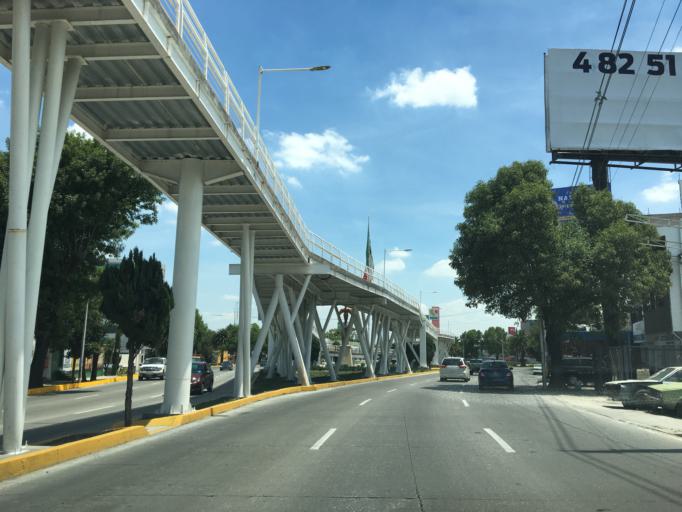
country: MX
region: Puebla
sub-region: Cuautlancingo
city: Sanctorum
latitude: 19.0765
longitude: -98.2278
